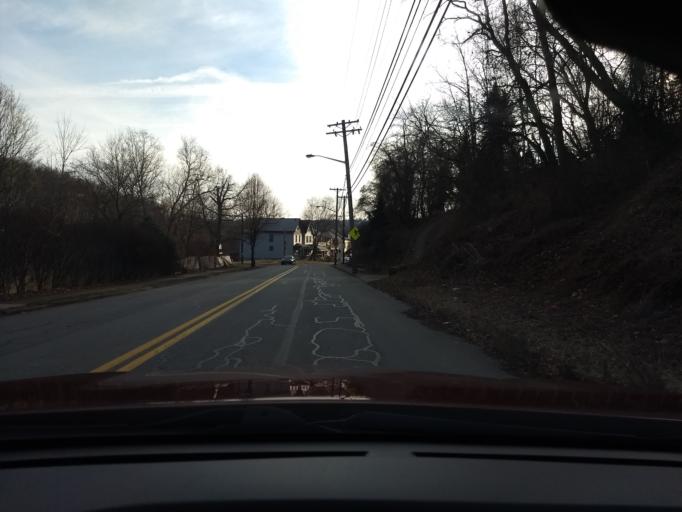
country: US
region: Pennsylvania
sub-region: Allegheny County
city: Homestead
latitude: 40.4141
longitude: -79.9394
